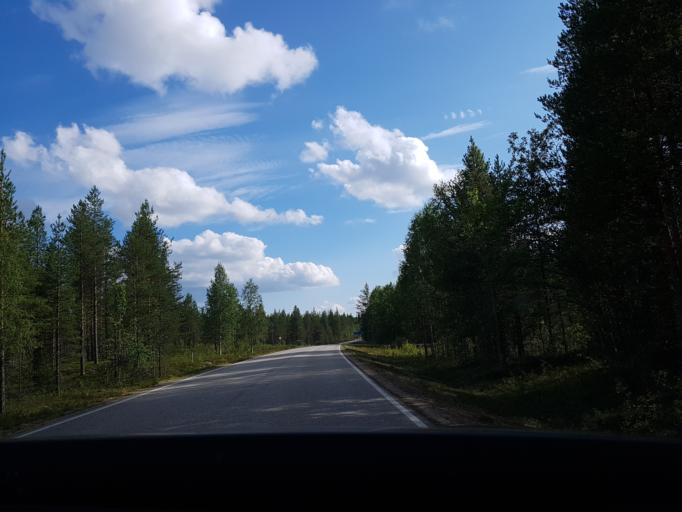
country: FI
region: Kainuu
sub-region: Kehys-Kainuu
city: Kuhmo
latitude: 64.6228
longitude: 29.6978
